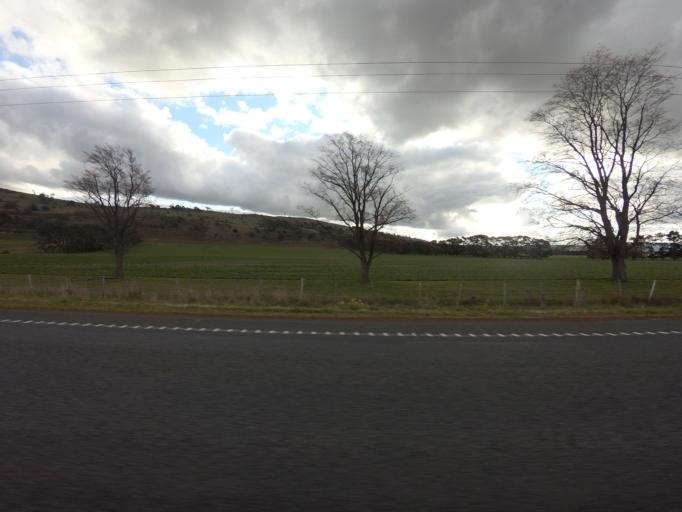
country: AU
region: Tasmania
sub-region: Northern Midlands
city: Evandale
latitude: -42.0444
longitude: 147.4824
